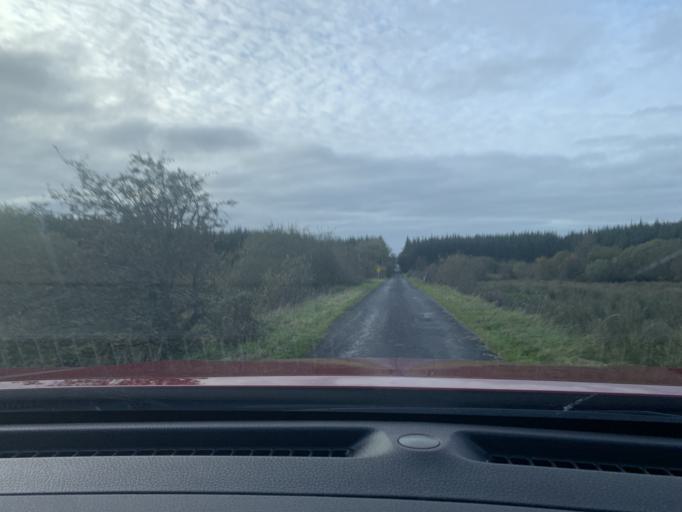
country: IE
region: Connaught
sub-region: Roscommon
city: Ballaghaderreen
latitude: 53.9674
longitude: -8.6149
